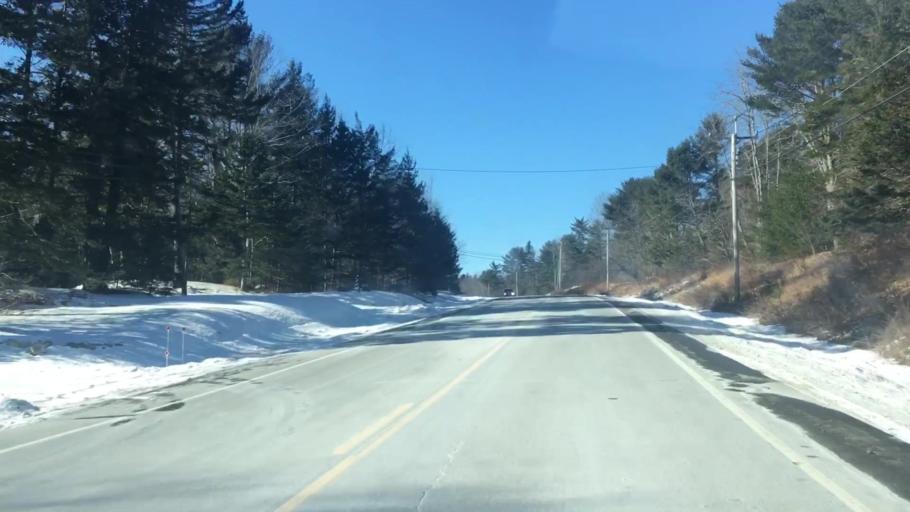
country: US
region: Maine
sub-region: Hancock County
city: Surry
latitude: 44.4944
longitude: -68.4678
